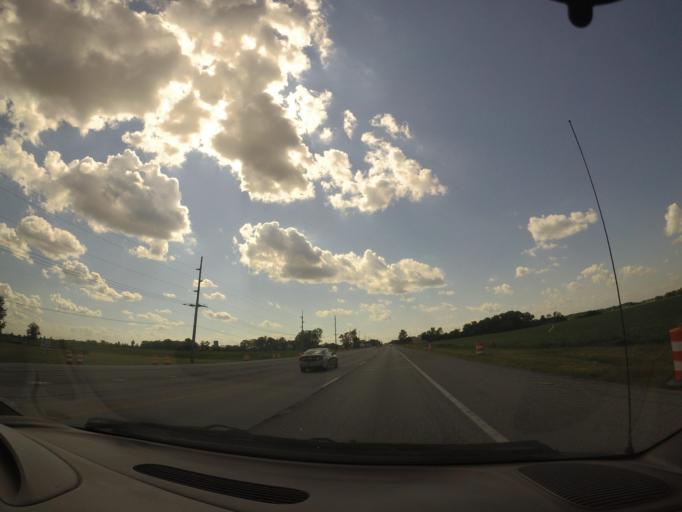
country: US
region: Ohio
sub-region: Sandusky County
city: Clyde
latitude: 41.3188
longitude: -83.0088
